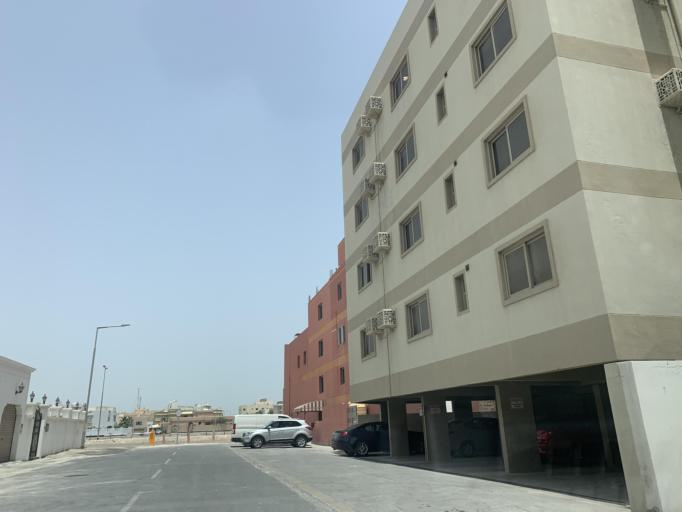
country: BH
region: Northern
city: Ar Rifa'
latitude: 26.1413
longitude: 50.5866
